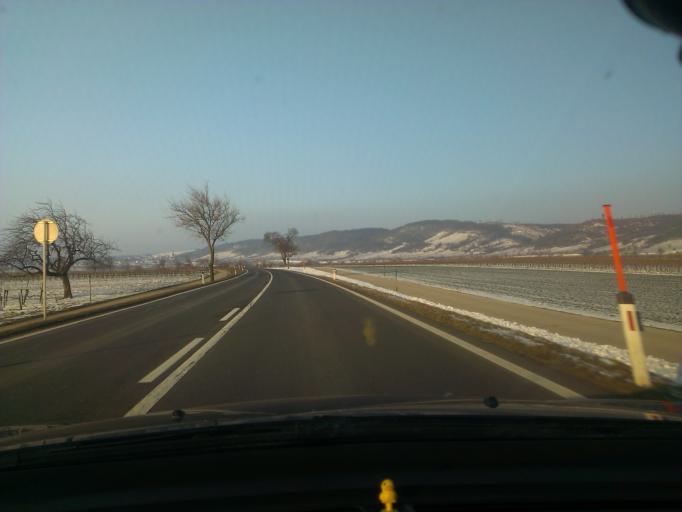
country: AT
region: Burgenland
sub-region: Eisenstadt-Umgebung
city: Donnerskirchen
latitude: 47.9090
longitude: 16.6740
